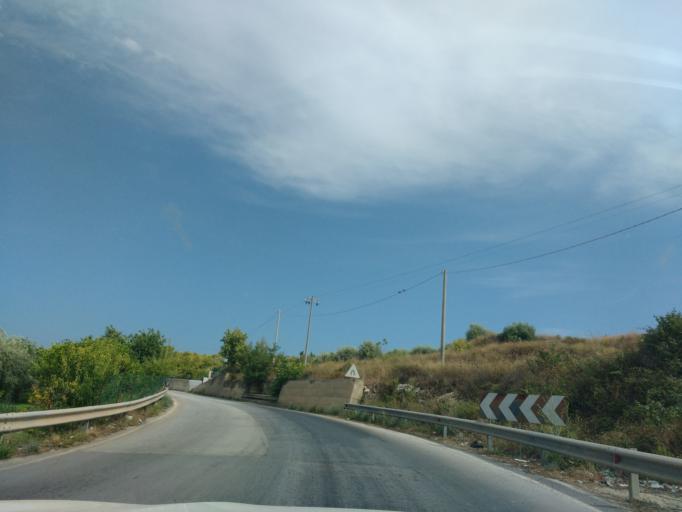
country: IT
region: Sicily
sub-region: Provincia di Siracusa
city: Noto
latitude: 36.8786
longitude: 15.0696
